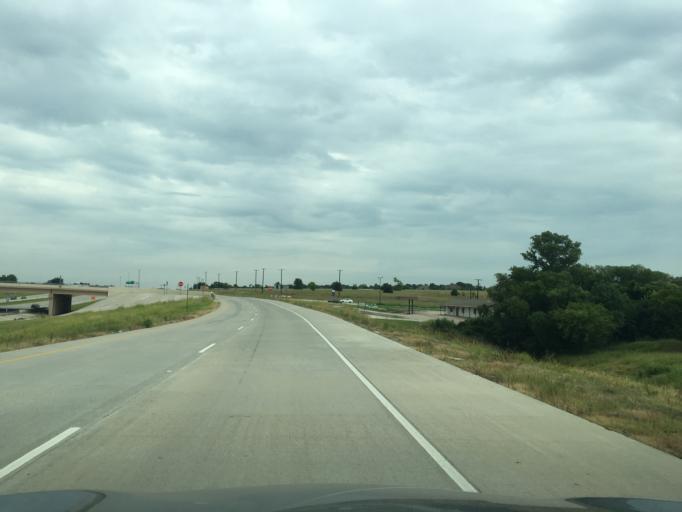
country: US
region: Texas
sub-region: Collin County
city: Melissa
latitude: 33.2832
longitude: -96.5917
